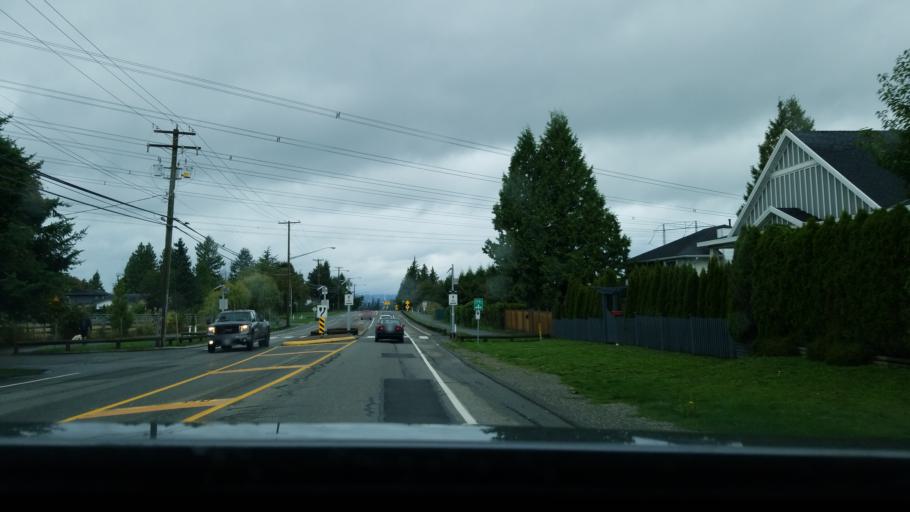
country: CA
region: British Columbia
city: Langley
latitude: 49.1188
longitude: -122.7179
